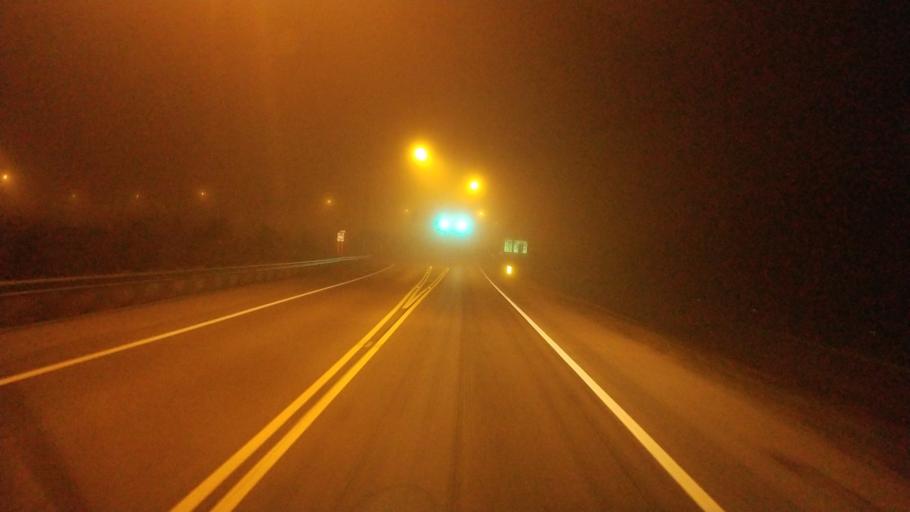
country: US
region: Ohio
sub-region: Scioto County
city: West Portsmouth
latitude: 38.7402
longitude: -83.0233
